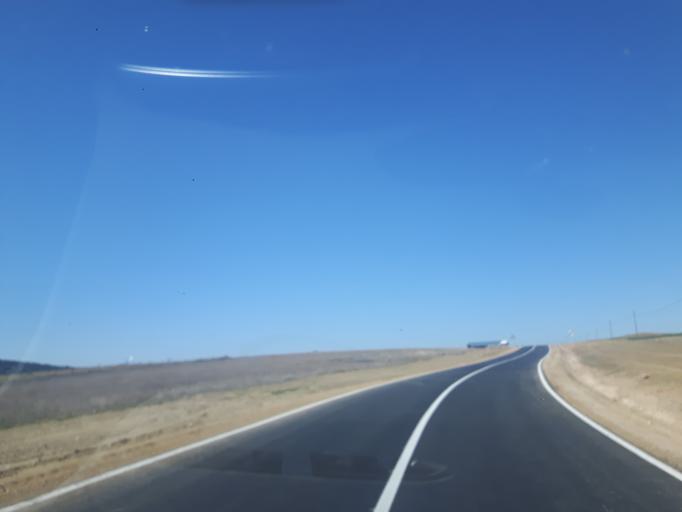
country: ES
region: Castille and Leon
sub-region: Provincia de Salamanca
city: Terradillos
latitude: 40.8229
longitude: -5.5331
